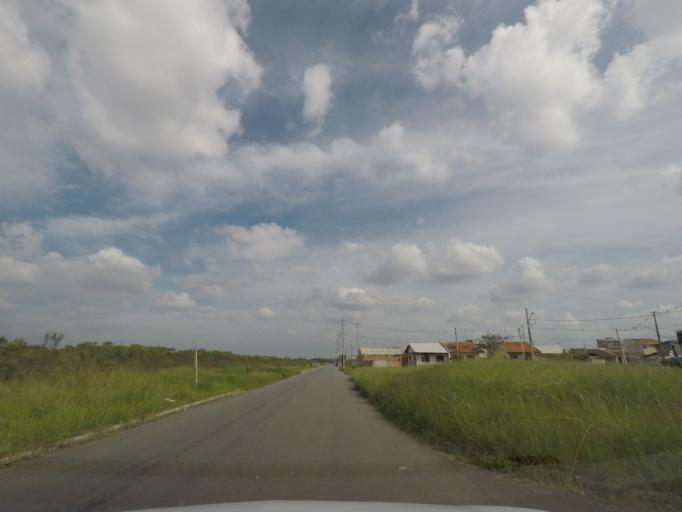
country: BR
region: Parana
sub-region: Sao Jose Dos Pinhais
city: Sao Jose dos Pinhais
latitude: -25.4900
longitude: -49.1972
